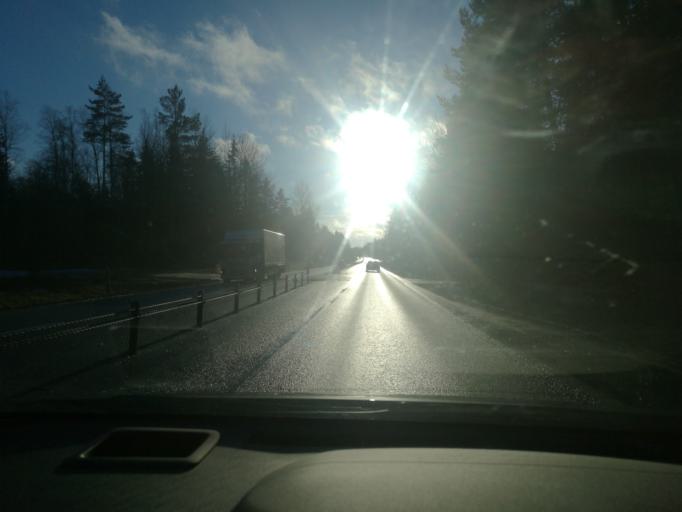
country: SE
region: OEstergoetland
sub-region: Norrkopings Kommun
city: Jursla
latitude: 58.7198
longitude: 16.1679
